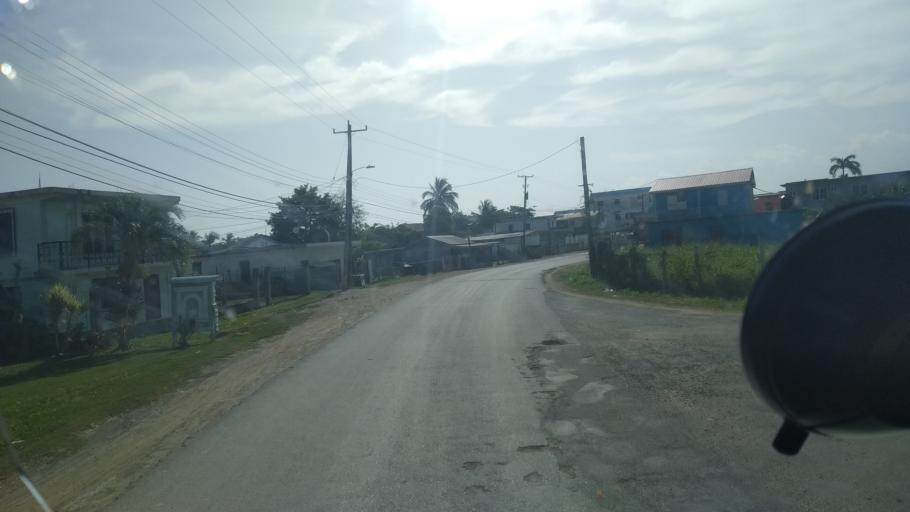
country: BZ
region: Corozal
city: Corozal
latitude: 18.3929
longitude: -88.3916
